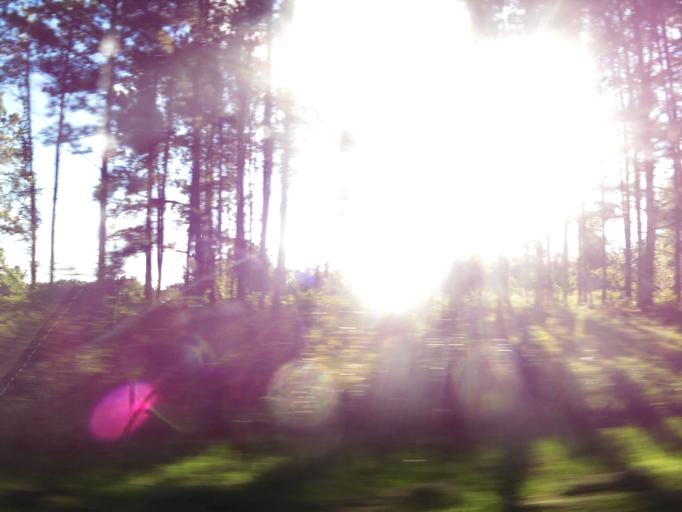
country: US
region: Florida
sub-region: Marion County
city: Citra
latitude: 29.4707
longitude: -82.1528
